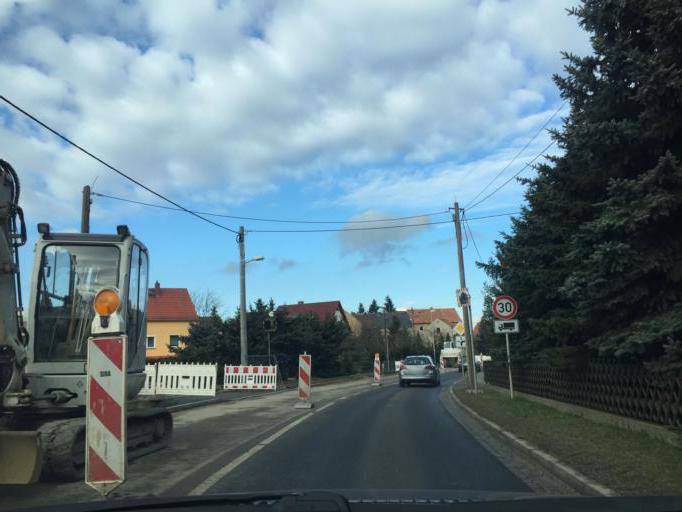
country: DE
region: Saxony
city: Radeburg
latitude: 51.1941
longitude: 13.7705
